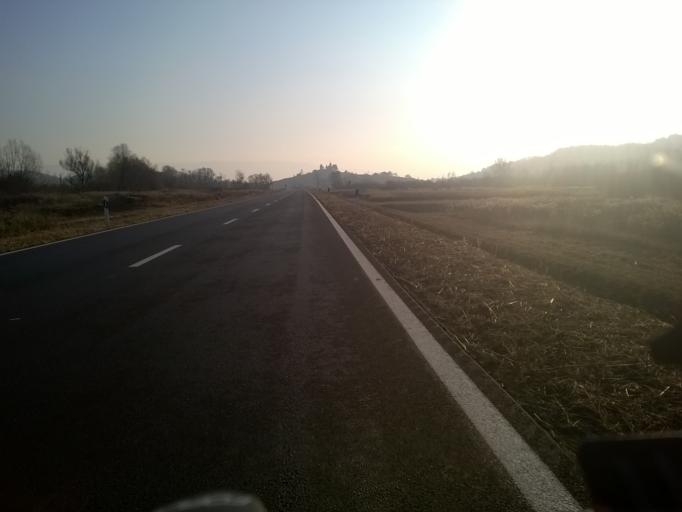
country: HR
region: Krapinsko-Zagorska
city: Zabok
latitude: 46.0504
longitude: 15.9132
